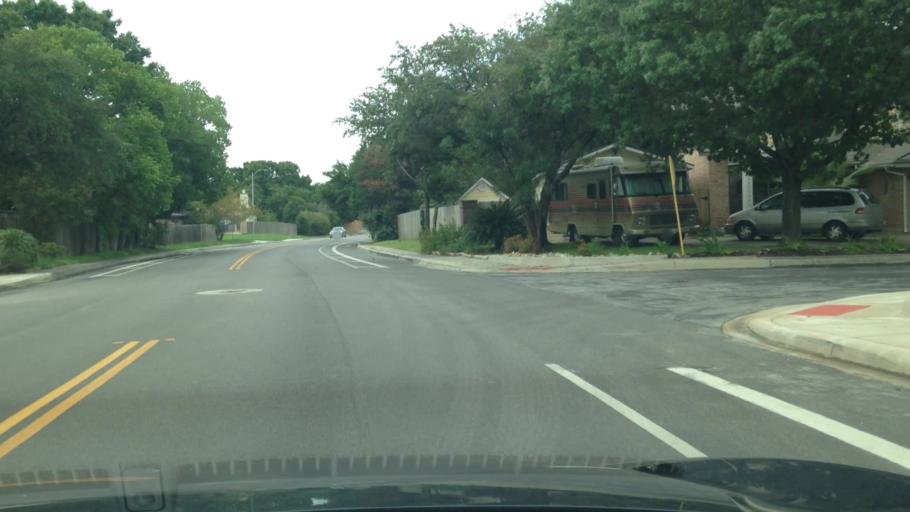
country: US
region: Texas
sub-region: Bexar County
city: Hollywood Park
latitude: 29.5722
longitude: -98.4284
